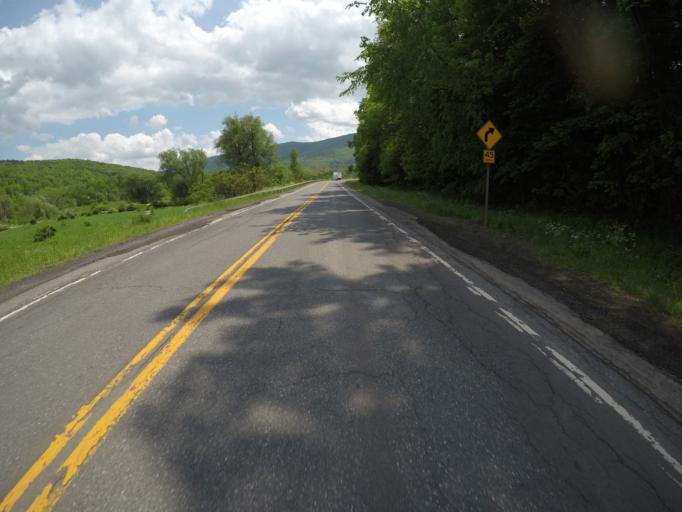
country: US
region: New York
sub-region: Delaware County
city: Stamford
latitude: 42.1572
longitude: -74.6244
